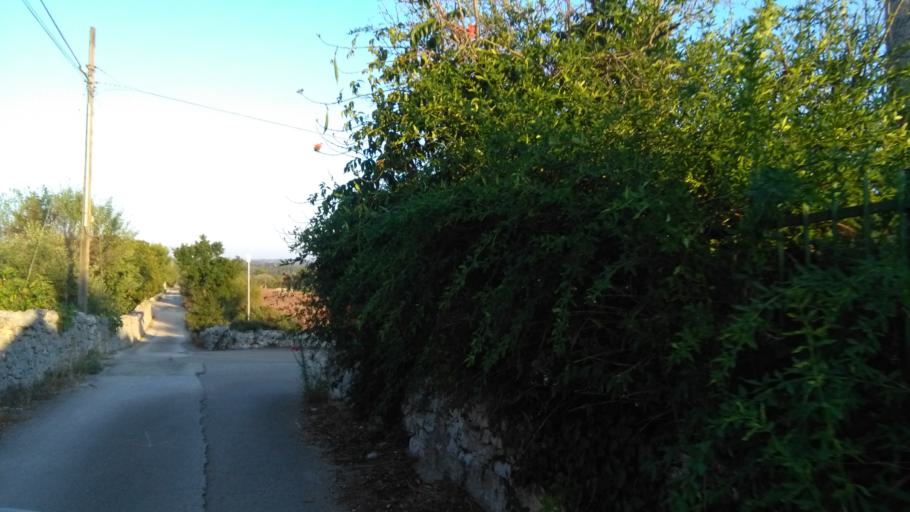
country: IT
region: Apulia
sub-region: Provincia di Bari
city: Putignano
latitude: 40.8242
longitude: 17.0988
